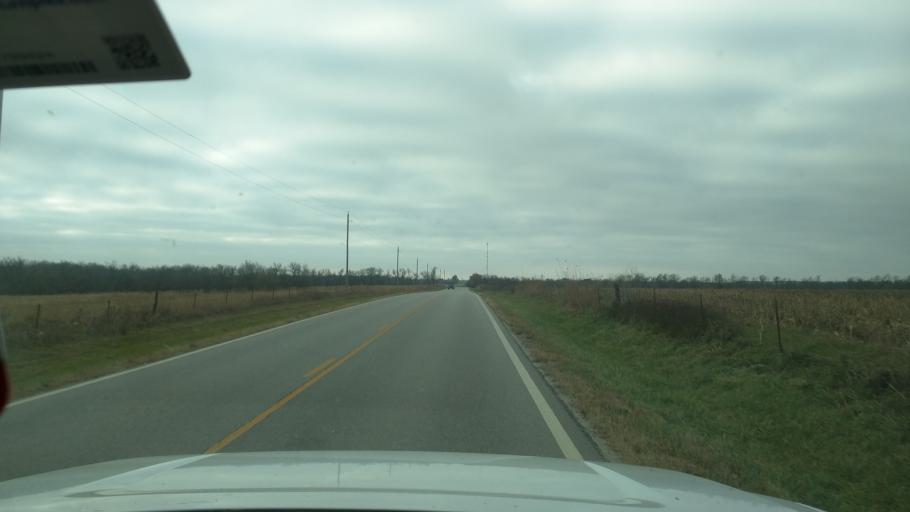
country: US
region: Kansas
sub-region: Elk County
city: Howard
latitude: 37.6466
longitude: -96.2346
